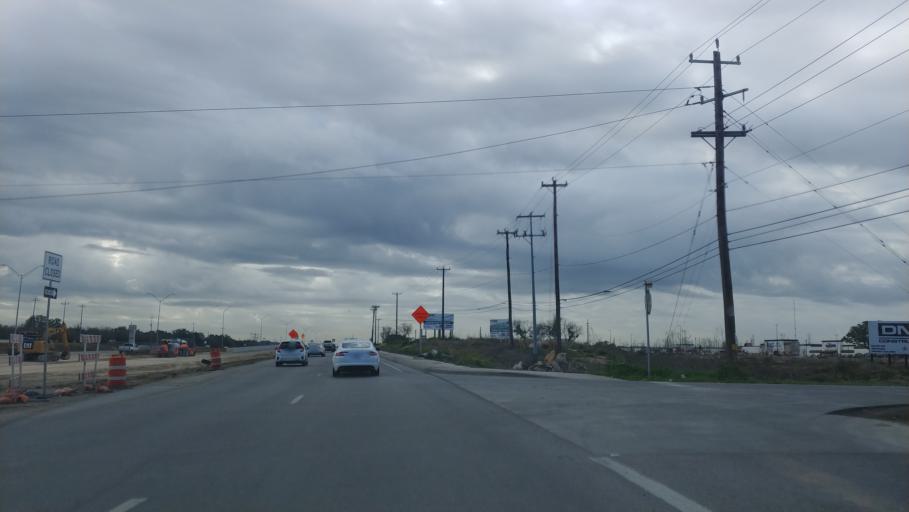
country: US
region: Texas
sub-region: Bexar County
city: Lackland Air Force Base
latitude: 29.4330
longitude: -98.7120
